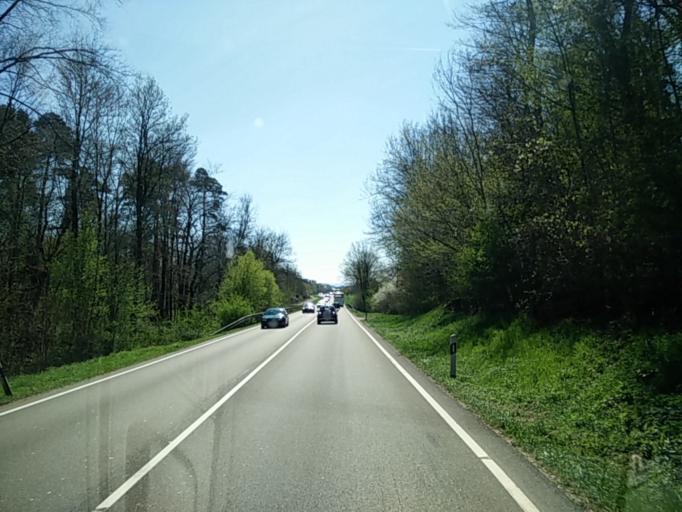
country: DE
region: Baden-Wuerttemberg
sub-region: Tuebingen Region
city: Bodelshausen
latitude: 48.3942
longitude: 9.0024
